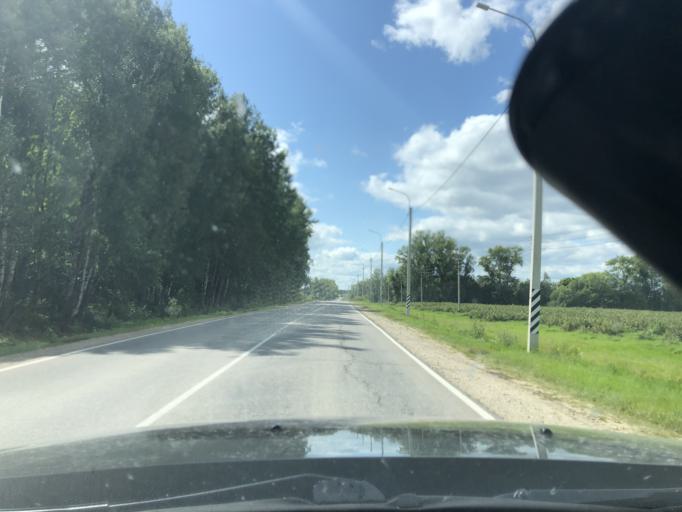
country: RU
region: Tula
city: Revyakino
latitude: 54.3428
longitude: 37.5824
